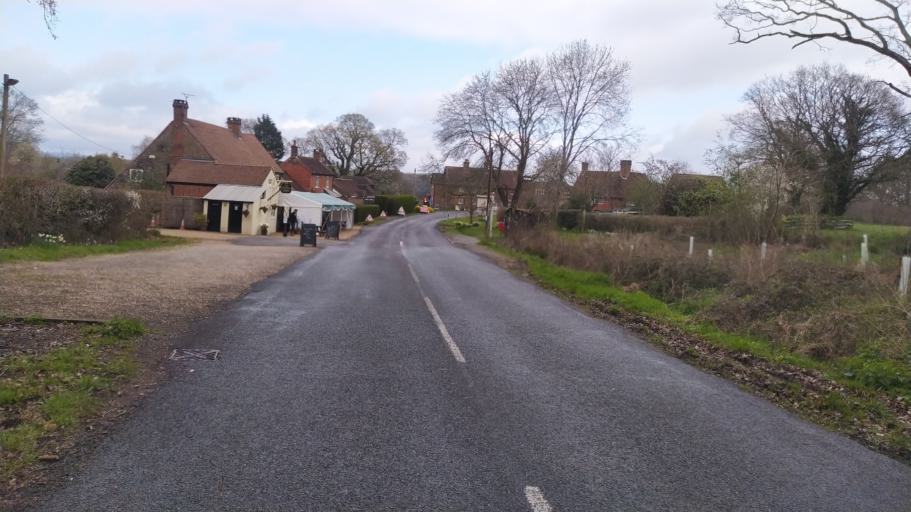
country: GB
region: England
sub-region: West Sussex
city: Petworth
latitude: 51.0267
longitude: -0.5940
